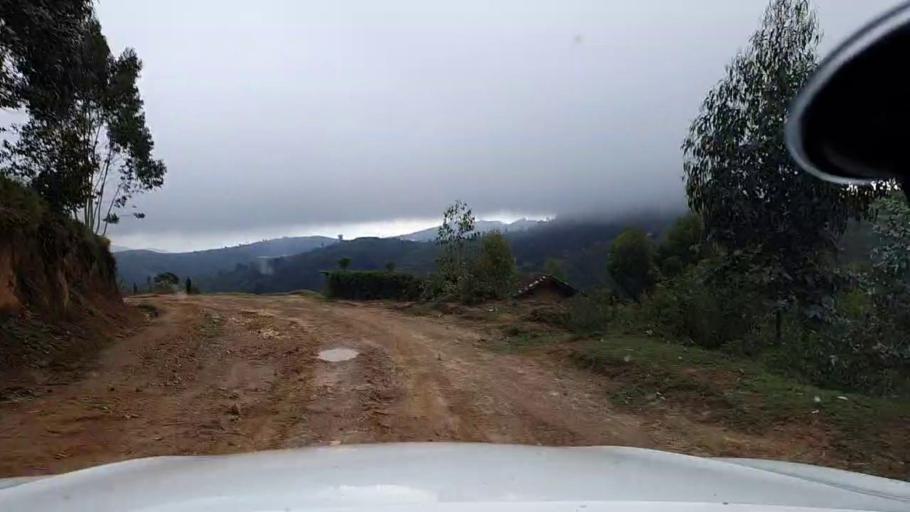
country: RW
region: Western Province
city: Kibuye
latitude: -2.0836
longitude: 29.5053
